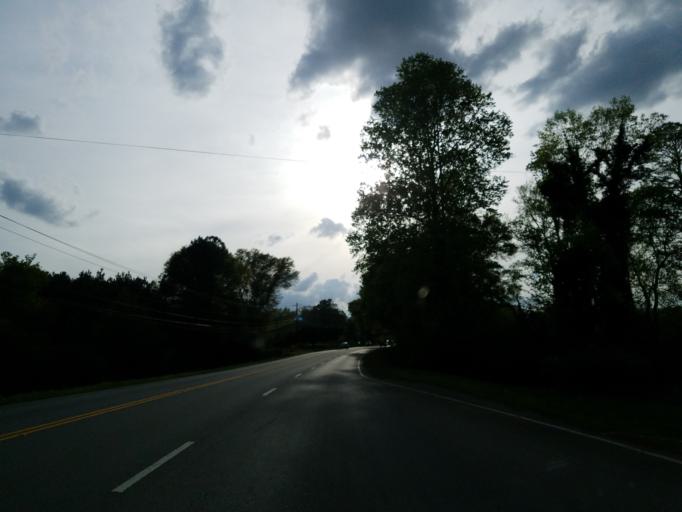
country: US
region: Georgia
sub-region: Cherokee County
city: Ball Ground
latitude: 34.2559
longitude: -84.3315
